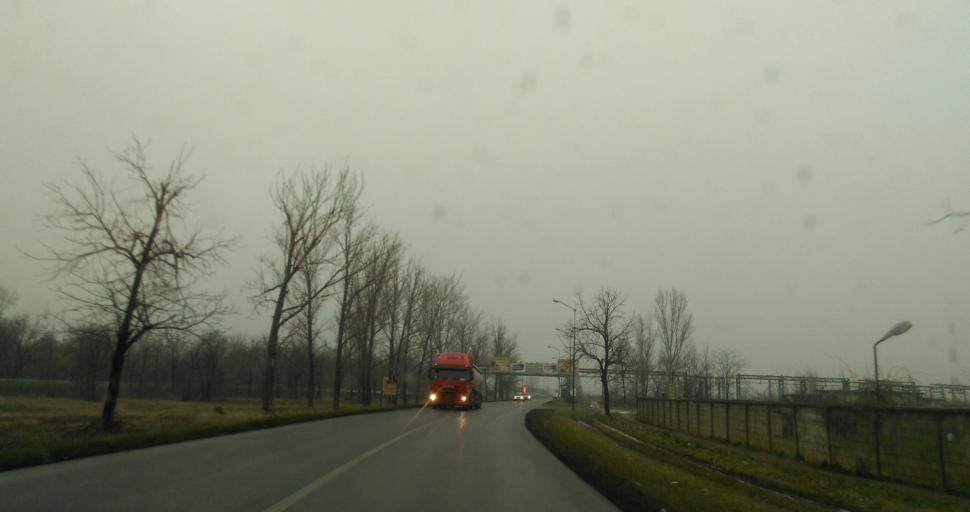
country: RS
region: Autonomna Pokrajina Vojvodina
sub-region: Srednjebanatski Okrug
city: Zrenjanin
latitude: 45.3674
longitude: 20.4224
